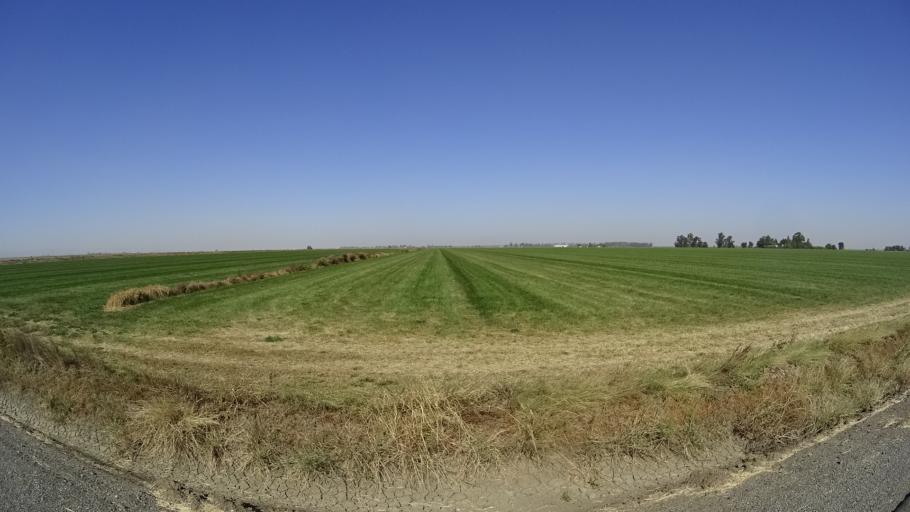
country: US
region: California
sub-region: Yolo County
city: Winters
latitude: 38.5906
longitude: -121.8846
